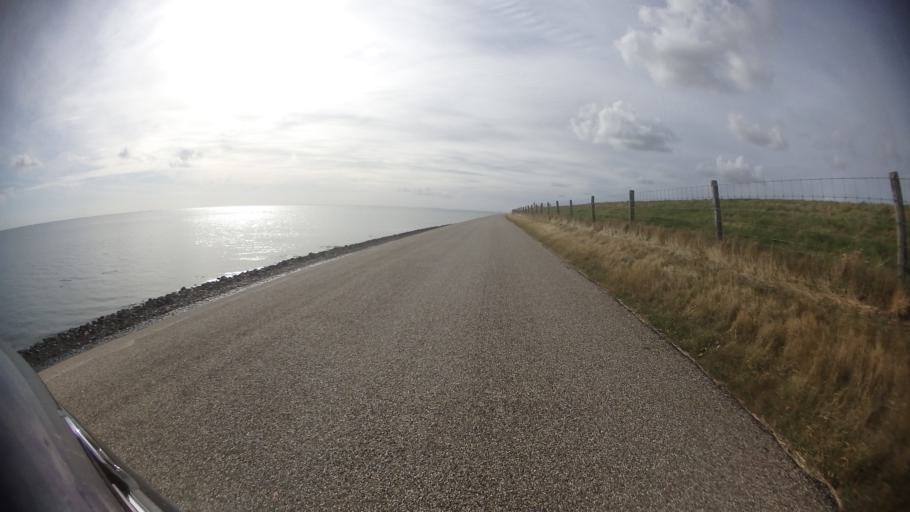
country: NL
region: North Holland
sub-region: Gemeente Texel
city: Den Burg
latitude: 53.0851
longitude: 4.8999
